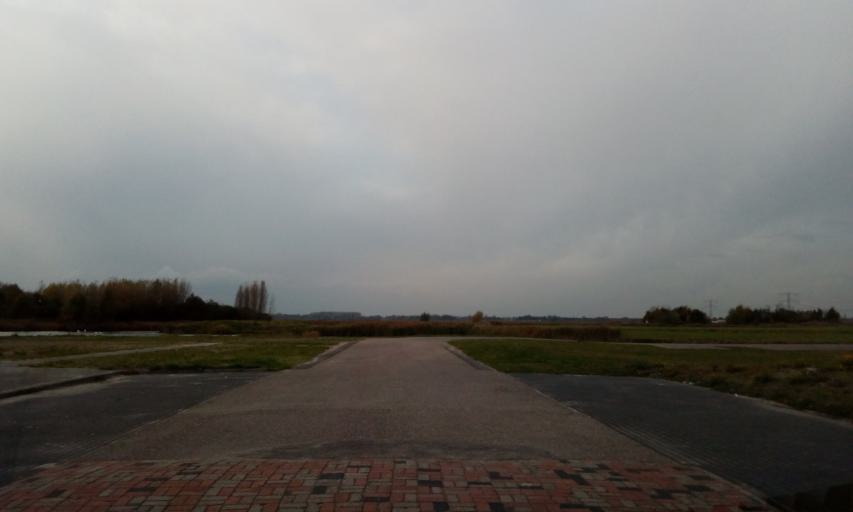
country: NL
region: South Holland
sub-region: Gemeente Lansingerland
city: Bleiswijk
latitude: 51.9864
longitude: 4.5801
